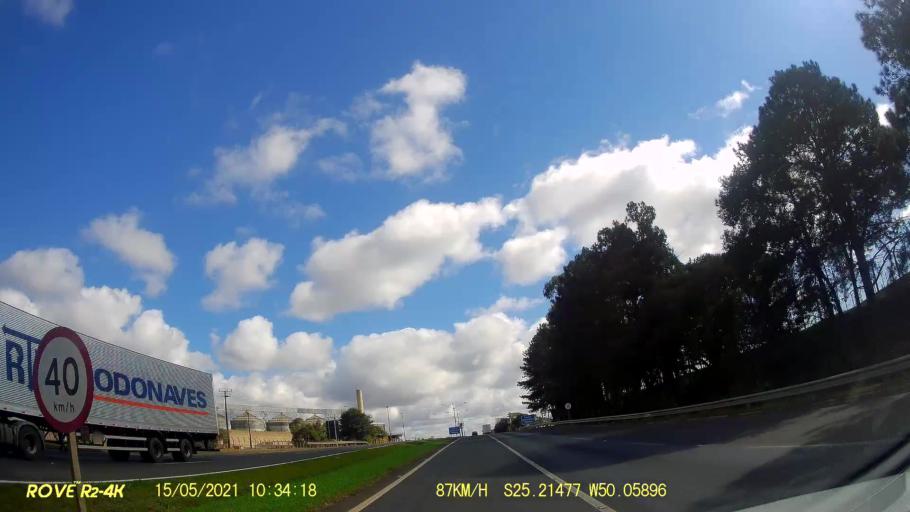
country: BR
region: Parana
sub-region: Ponta Grossa
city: Ponta Grossa
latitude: -25.2146
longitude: -50.0590
